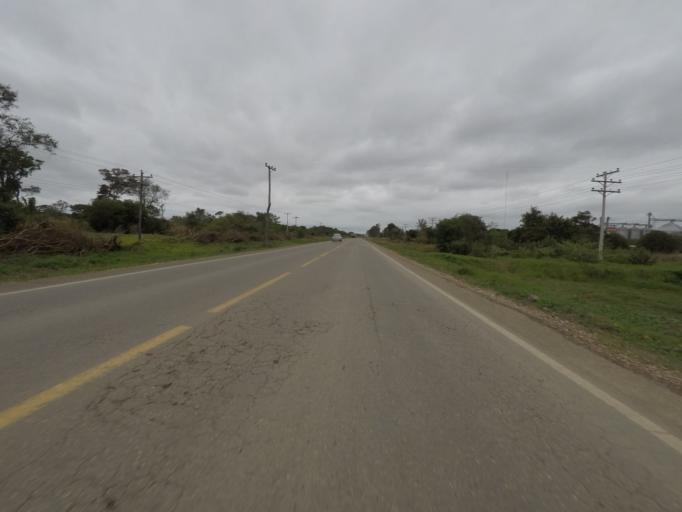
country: BO
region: Santa Cruz
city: Okinawa Numero Uno
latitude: -17.2187
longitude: -62.5565
